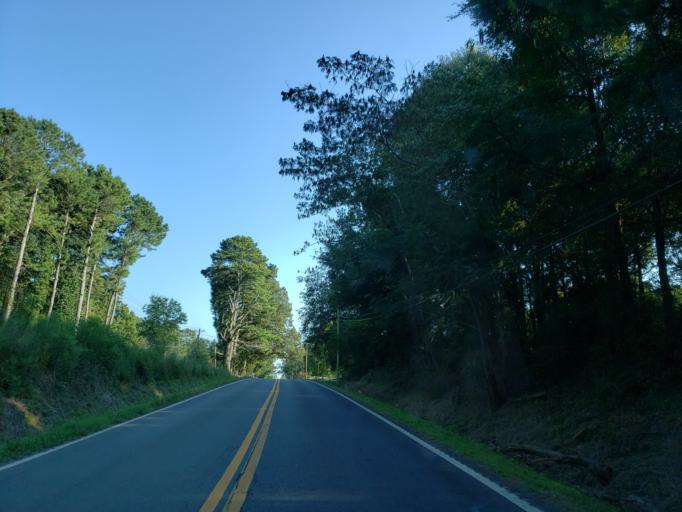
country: US
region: Tennessee
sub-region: Bradley County
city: Wildwood Lake
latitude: 35.0428
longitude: -84.8056
